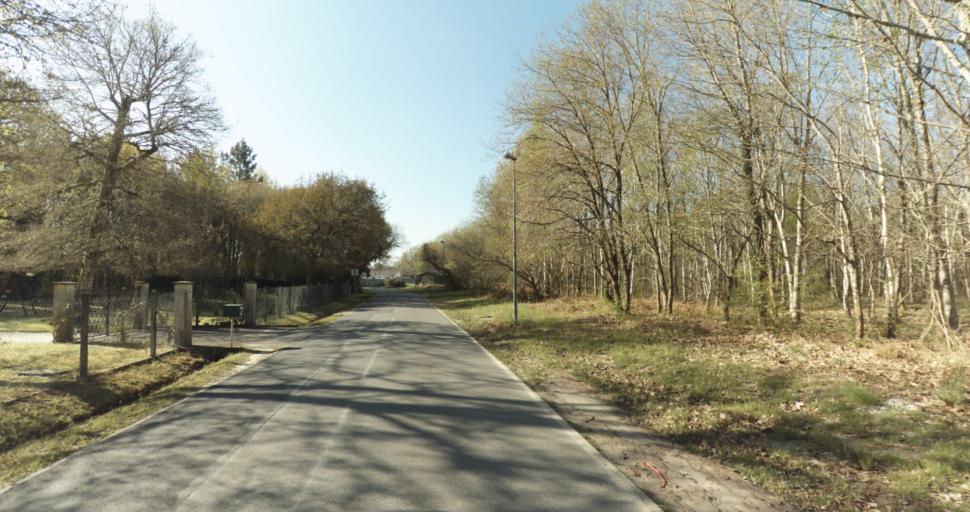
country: FR
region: Aquitaine
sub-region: Departement de la Gironde
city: Martignas-sur-Jalle
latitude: 44.8056
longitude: -0.8436
